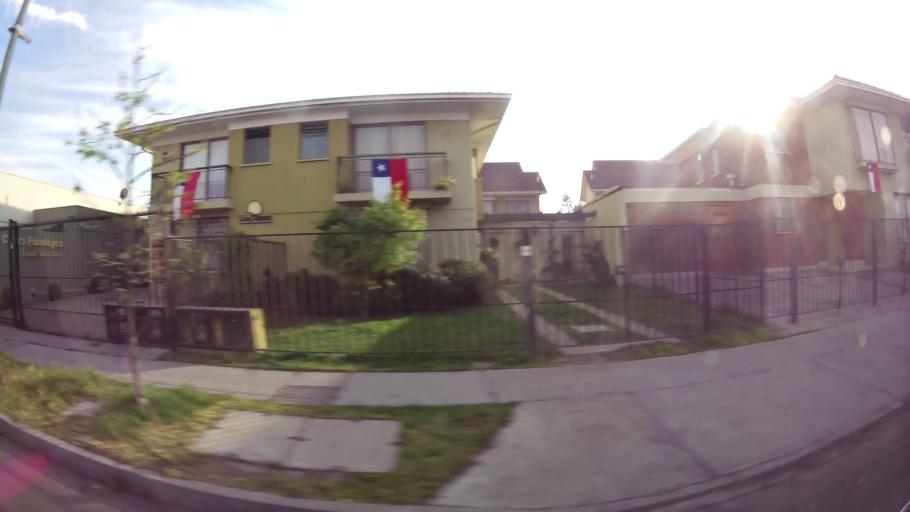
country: CL
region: Santiago Metropolitan
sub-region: Provincia de Maipo
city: San Bernardo
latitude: -33.5585
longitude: -70.7837
